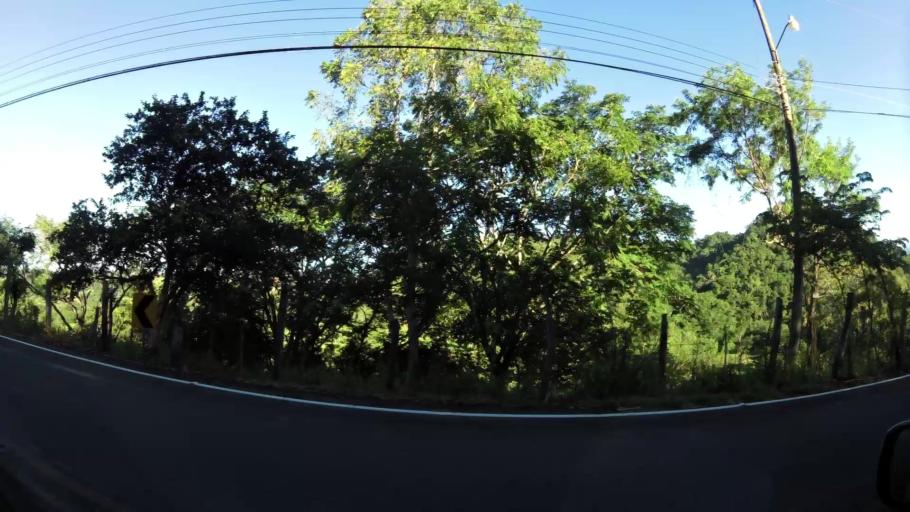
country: CR
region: Puntarenas
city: Miramar
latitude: 10.1772
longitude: -84.8455
